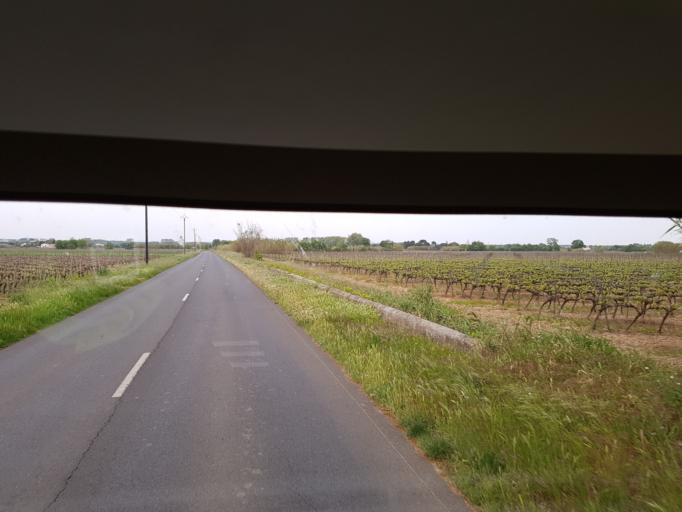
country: FR
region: Languedoc-Roussillon
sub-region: Departement de l'Herault
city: Villeneuve-les-Beziers
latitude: 43.3022
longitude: 3.2763
